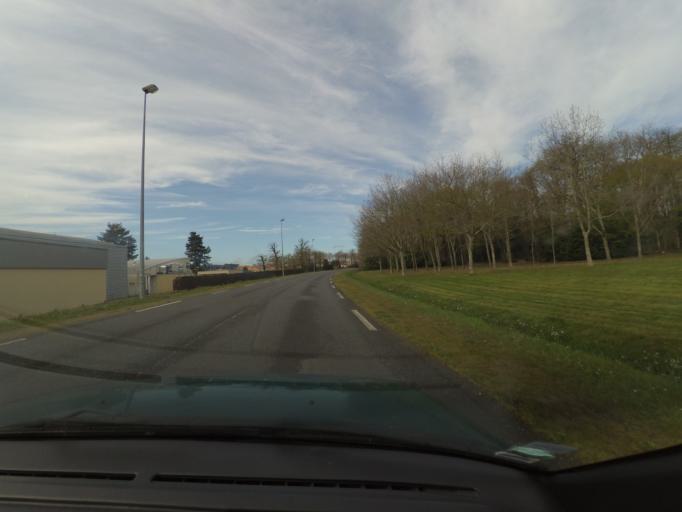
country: FR
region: Pays de la Loire
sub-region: Departement de la Loire-Atlantique
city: Aigrefeuille-sur-Maine
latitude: 47.0766
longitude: -1.4075
